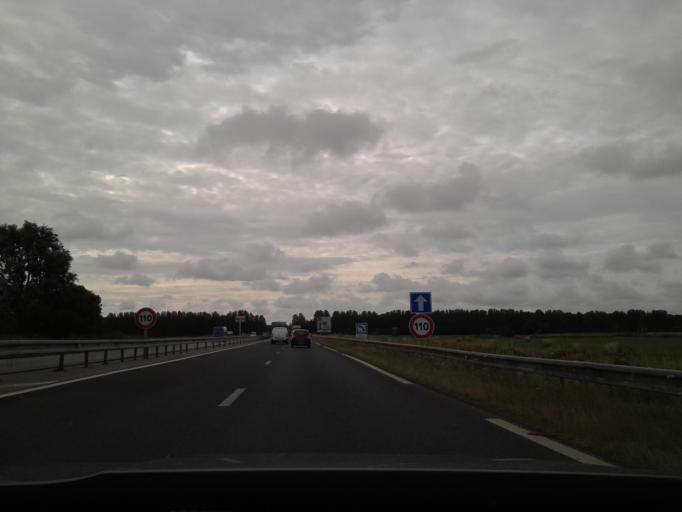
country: FR
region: Lower Normandy
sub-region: Departement de la Manche
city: Carentan
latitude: 49.3181
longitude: -1.2378
